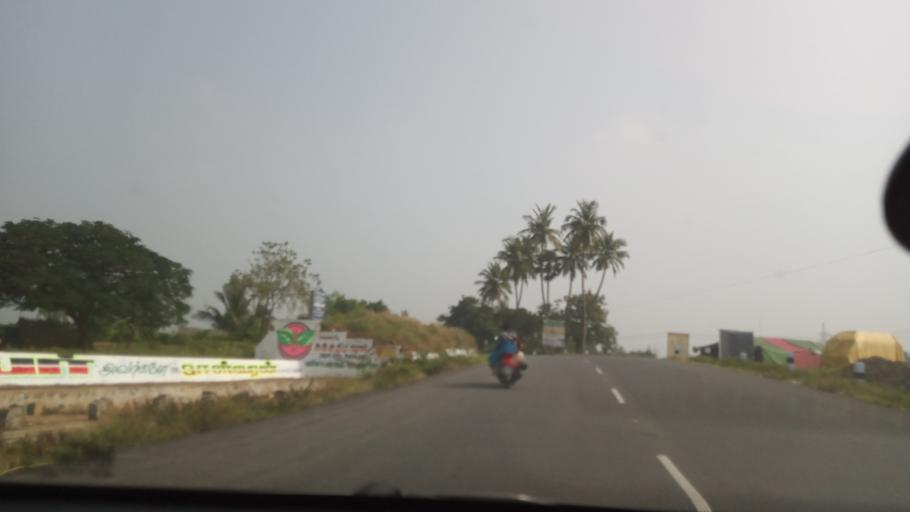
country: IN
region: Tamil Nadu
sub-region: Erode
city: Punjai Puliyampatti
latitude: 11.3969
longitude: 77.1830
